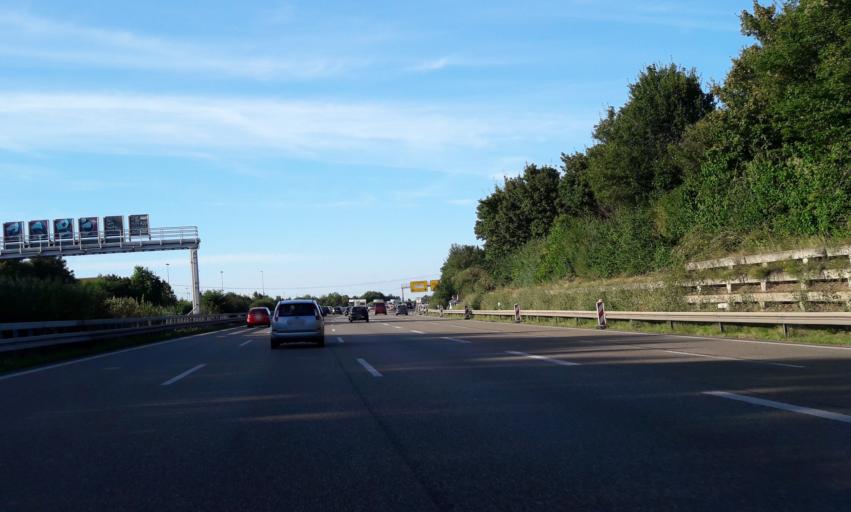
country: DE
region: Baden-Wuerttemberg
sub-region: Regierungsbezirk Stuttgart
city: Asperg
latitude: 48.9149
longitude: 9.1548
